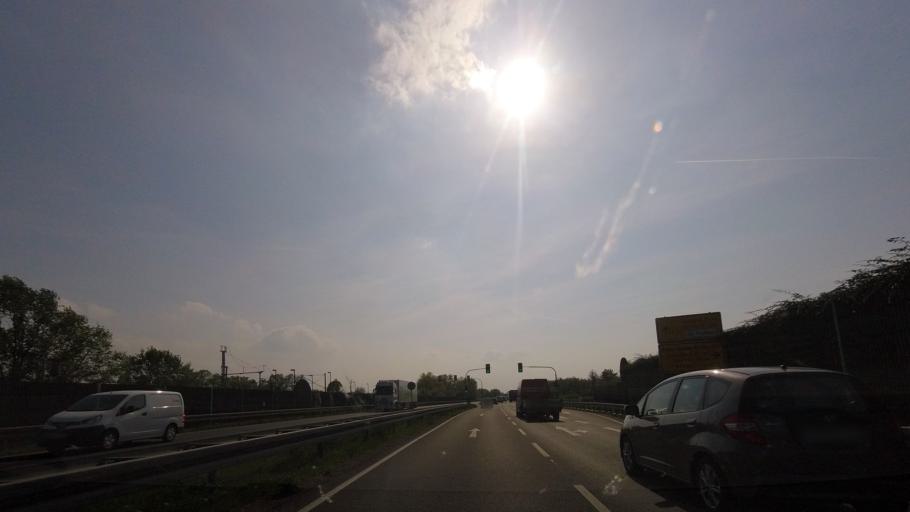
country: DE
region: Saxony-Anhalt
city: Wittenburg
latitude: 51.8443
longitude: 12.6374
